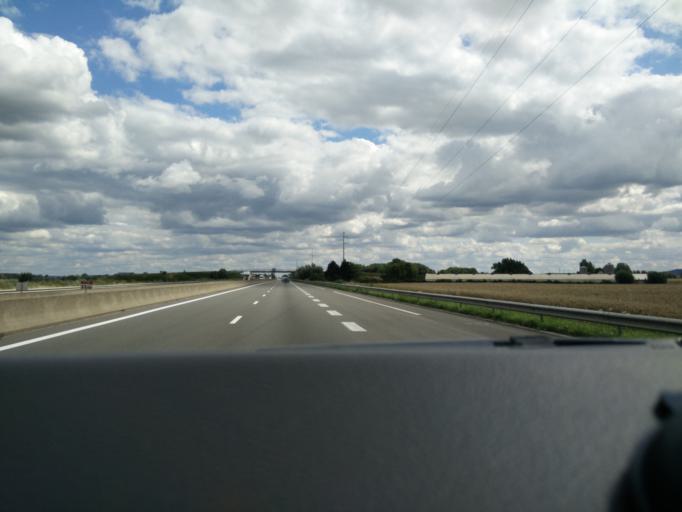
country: FR
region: Nord-Pas-de-Calais
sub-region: Departement du Nord
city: Herzeele
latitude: 50.8818
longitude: 2.5186
